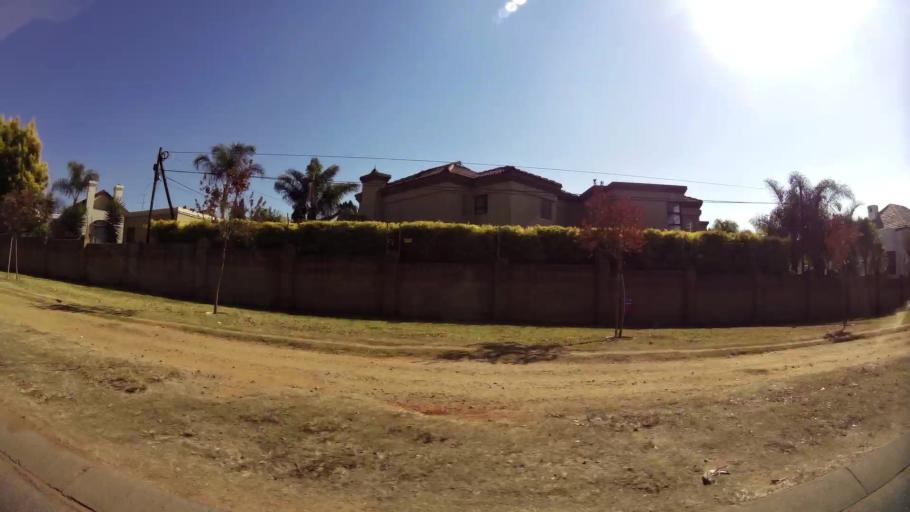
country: ZA
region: Gauteng
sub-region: Ekurhuleni Metropolitan Municipality
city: Tembisa
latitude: -26.0690
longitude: 28.2497
